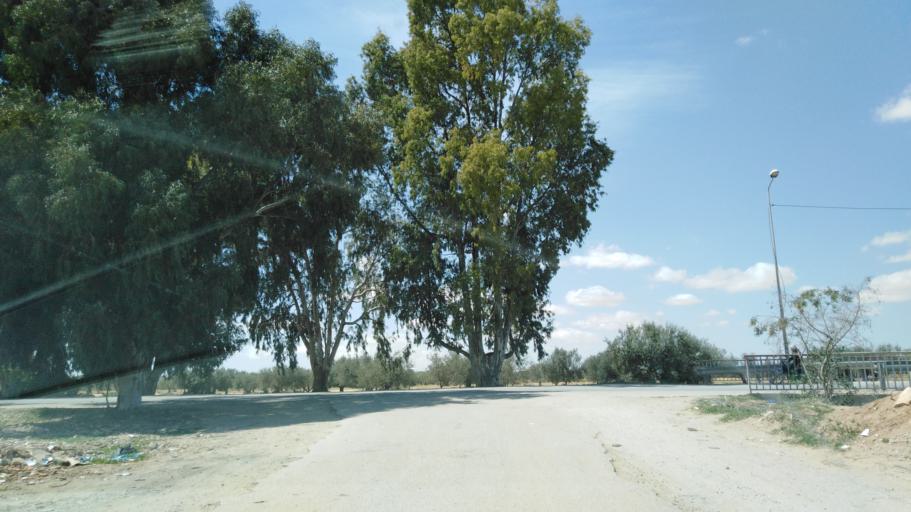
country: TN
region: Safaqis
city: Sfax
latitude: 34.7374
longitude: 10.5306
